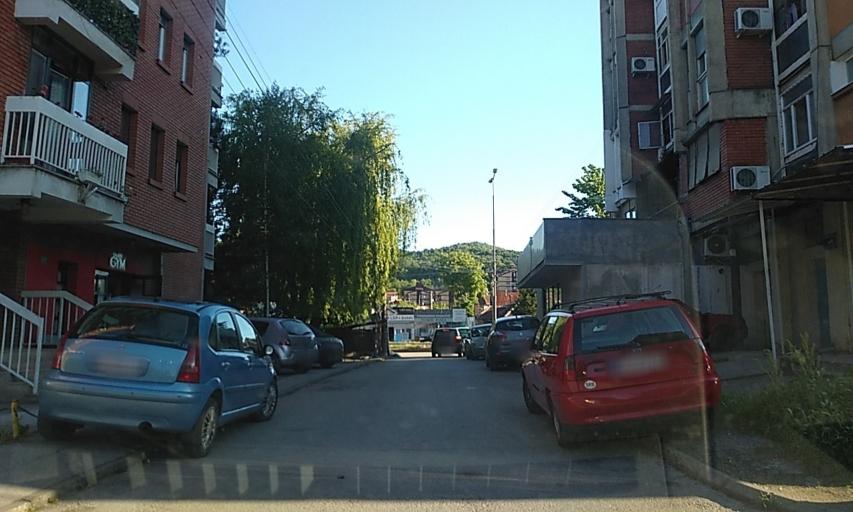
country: RS
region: Central Serbia
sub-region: Nisavski Okrug
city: Nis
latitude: 43.3117
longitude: 21.9304
